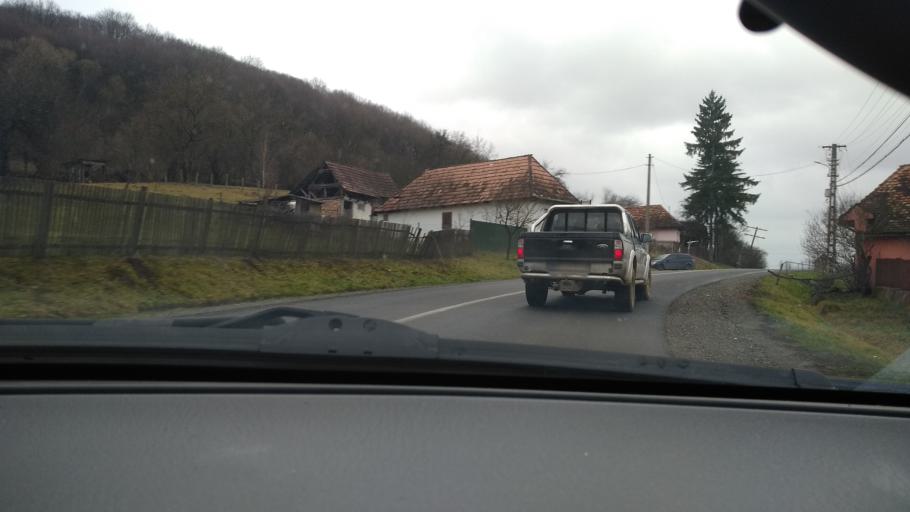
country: RO
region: Mures
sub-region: Comuna Bereni
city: Bereni
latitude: 46.5553
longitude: 24.8680
